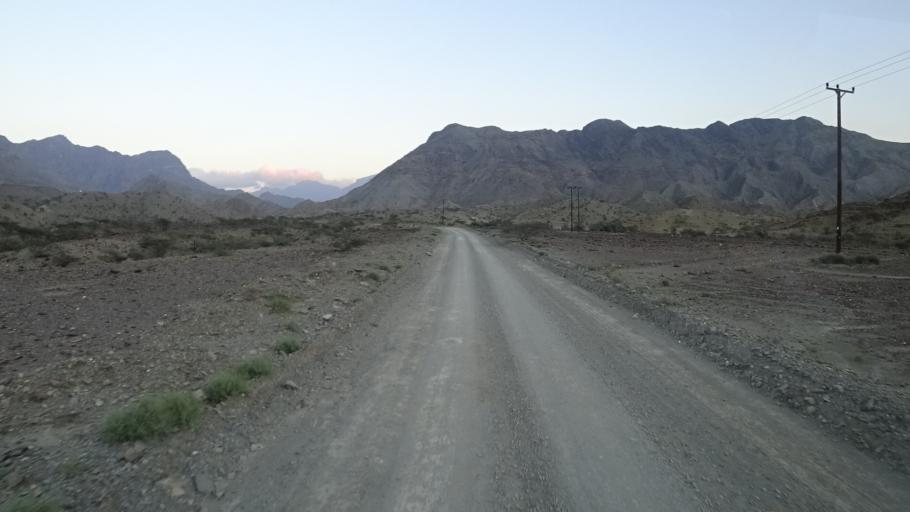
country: OM
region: Al Batinah
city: Rustaq
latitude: 23.2764
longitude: 57.3582
